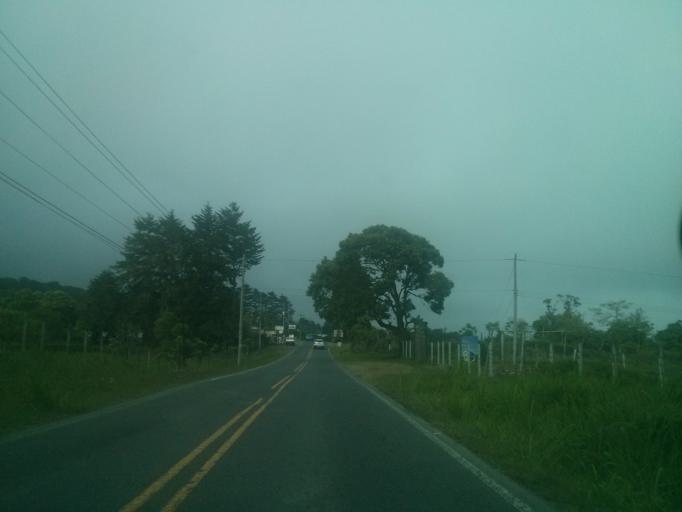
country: CR
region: Cartago
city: Cot
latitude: 9.8787
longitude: -83.8203
